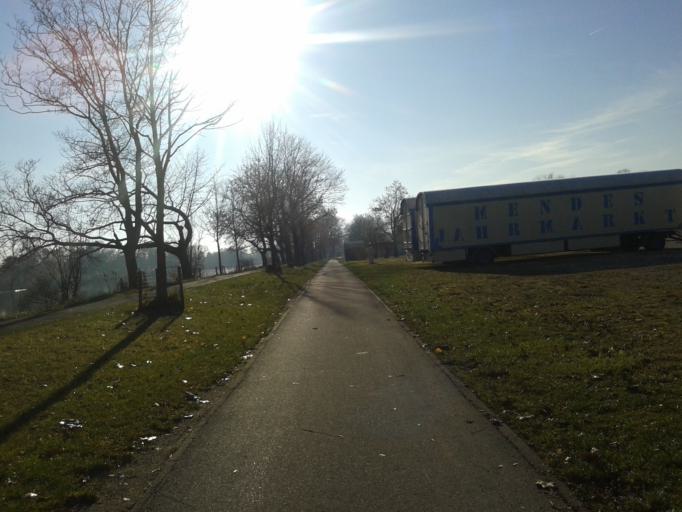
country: DE
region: Bavaria
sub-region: Swabia
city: Neu-Ulm
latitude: 48.4117
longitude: 10.0160
